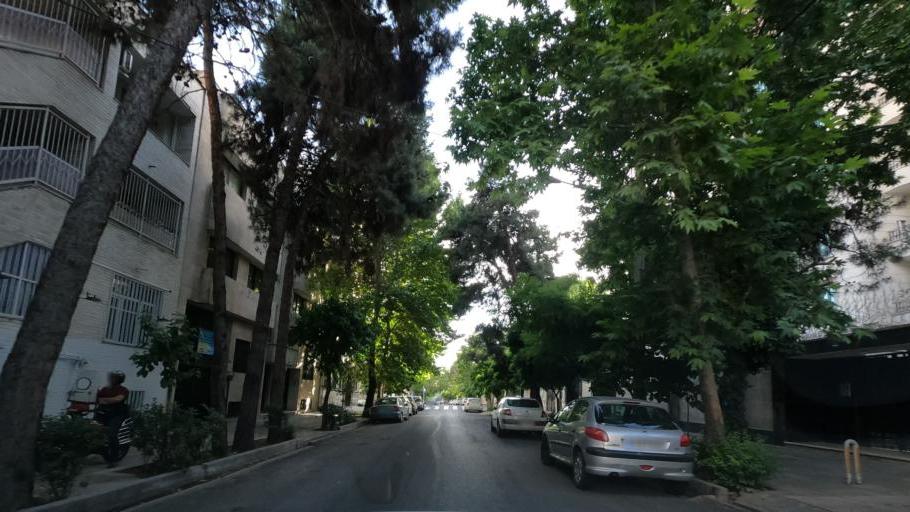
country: IR
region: Tehran
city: Tehran
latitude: 35.7353
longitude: 51.4083
